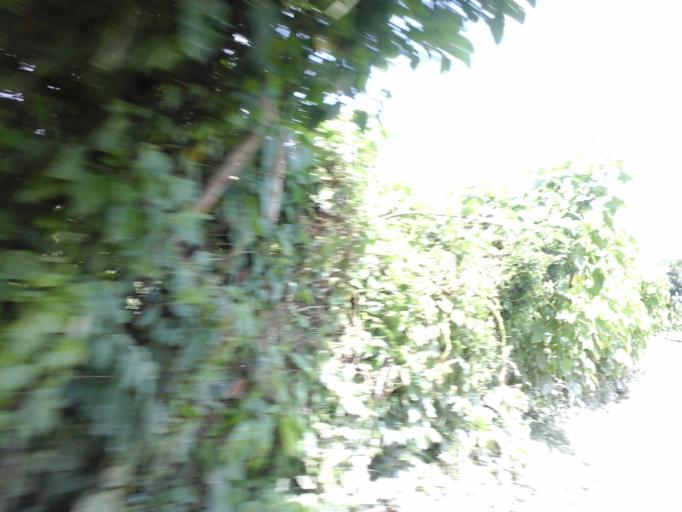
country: CO
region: Bolivar
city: San Pablo
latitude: 10.1539
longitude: -75.2735
